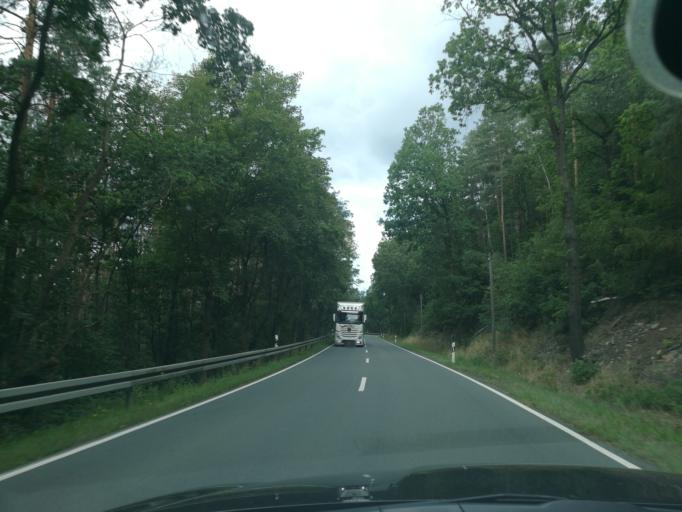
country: DE
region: Saxony
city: Oelsnitz
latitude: 50.3838
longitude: 12.1994
